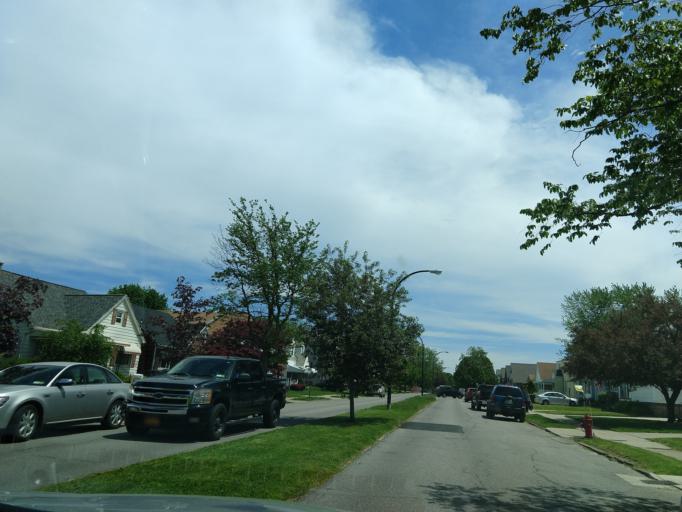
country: US
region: New York
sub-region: Erie County
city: Lackawanna
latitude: 42.8396
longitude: -78.8222
